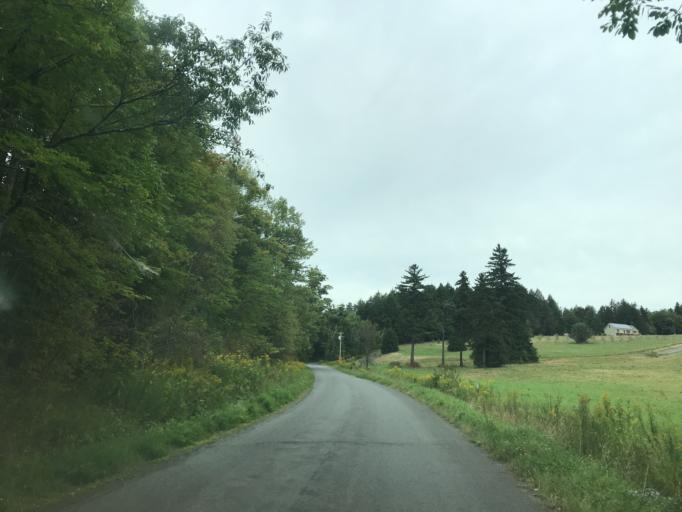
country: US
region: New York
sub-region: Otsego County
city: Worcester
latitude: 42.5772
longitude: -74.6718
